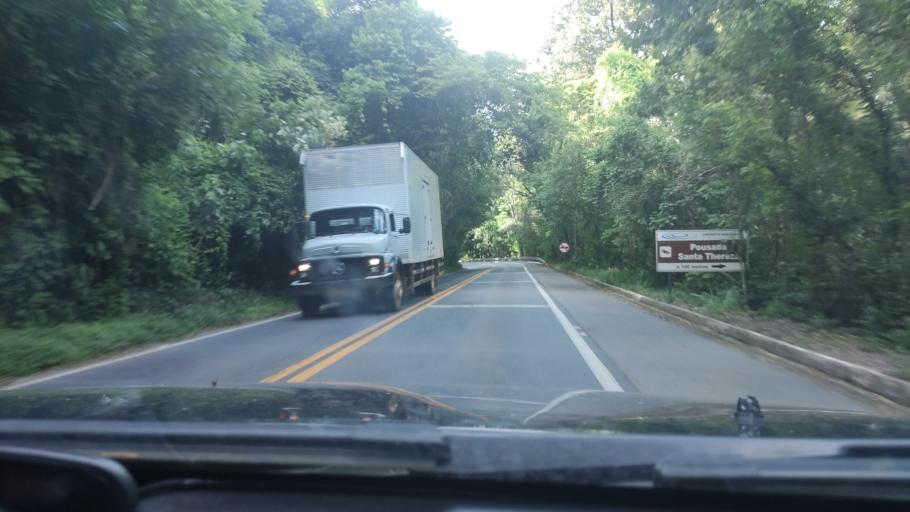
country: BR
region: Sao Paulo
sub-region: Aguas De Lindoia
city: Aguas de Lindoia
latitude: -22.5456
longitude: -46.6244
